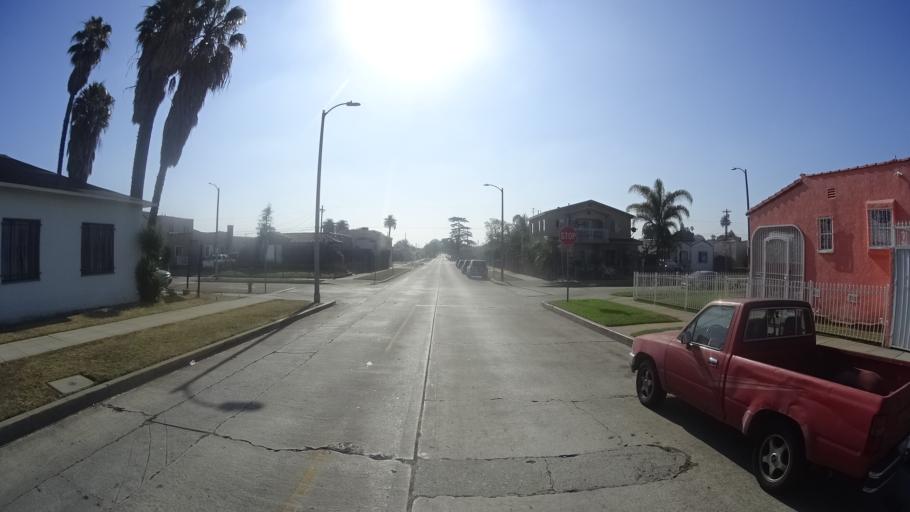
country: US
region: California
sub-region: Los Angeles County
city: View Park-Windsor Hills
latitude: 33.9782
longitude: -118.3220
